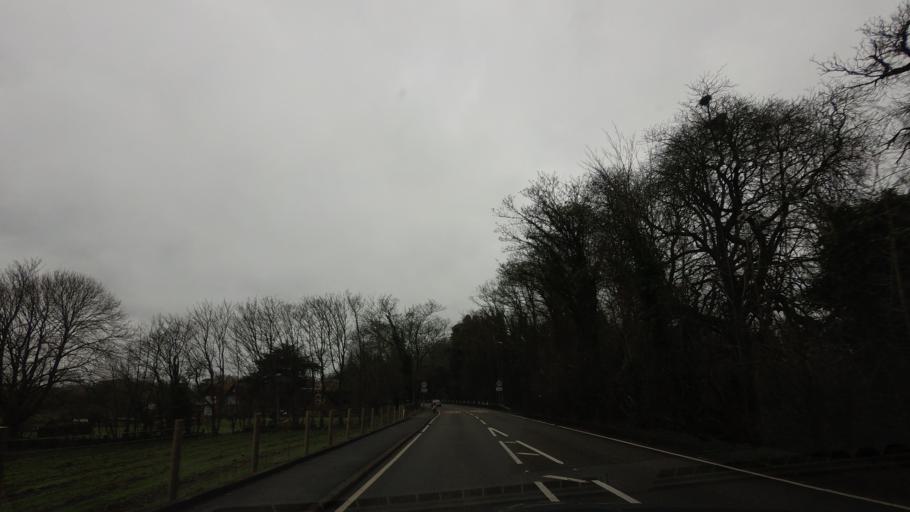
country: GB
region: England
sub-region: Kent
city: Maidstone
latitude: 51.2211
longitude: 0.5113
